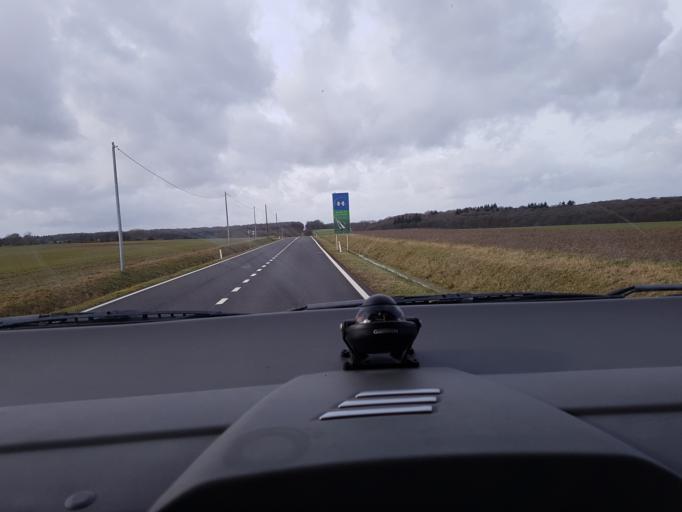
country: BE
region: Wallonia
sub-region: Province de Namur
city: Philippeville
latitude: 50.1968
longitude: 4.5083
